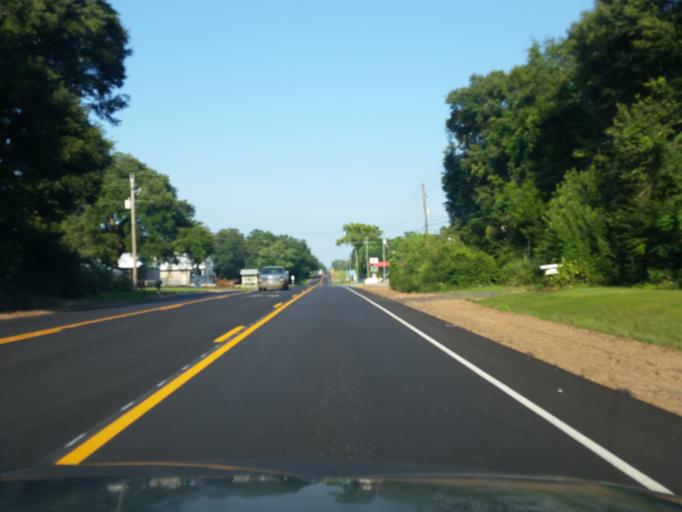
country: US
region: Alabama
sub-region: Baldwin County
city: Foley
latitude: 30.4065
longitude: -87.7697
